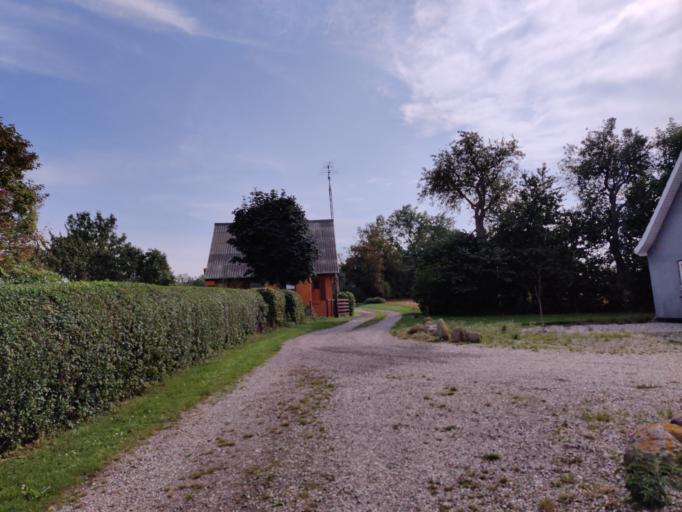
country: DK
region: Zealand
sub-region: Guldborgsund Kommune
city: Nykobing Falster
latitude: 54.7014
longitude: 11.9039
